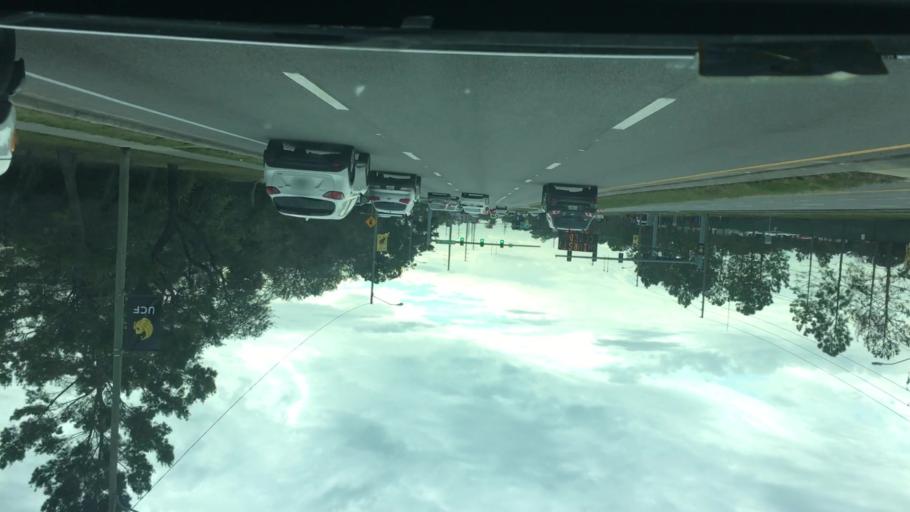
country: US
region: Florida
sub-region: Orange County
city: Alafaya
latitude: 28.6016
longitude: -81.2078
